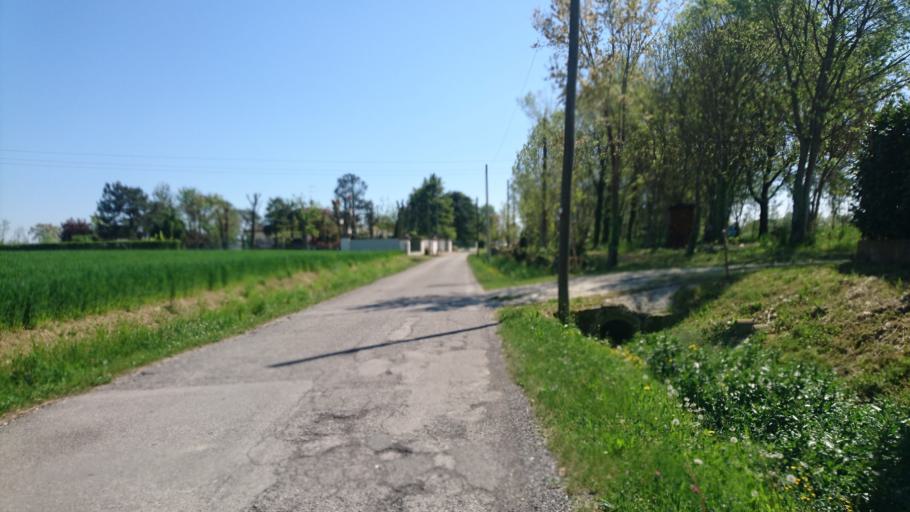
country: IT
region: Veneto
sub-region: Provincia di Treviso
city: Conscio
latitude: 45.6218
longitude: 12.2751
